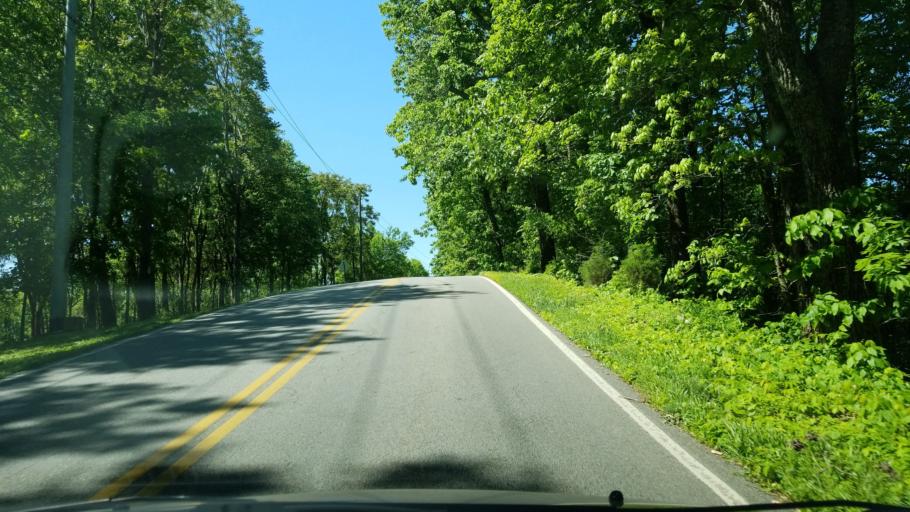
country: US
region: Tennessee
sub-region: Hamilton County
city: Middle Valley
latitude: 35.1576
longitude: -85.1886
